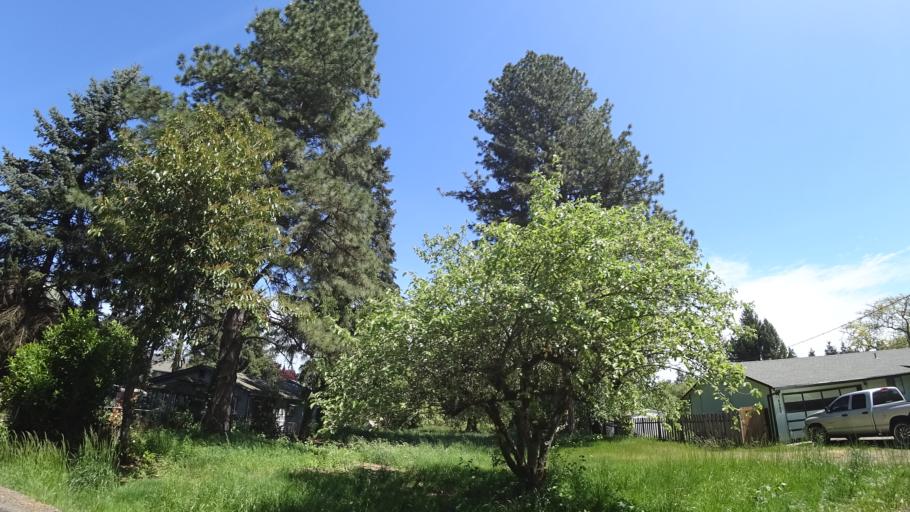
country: US
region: Oregon
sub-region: Washington County
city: Aloha
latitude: 45.4849
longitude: -122.8467
